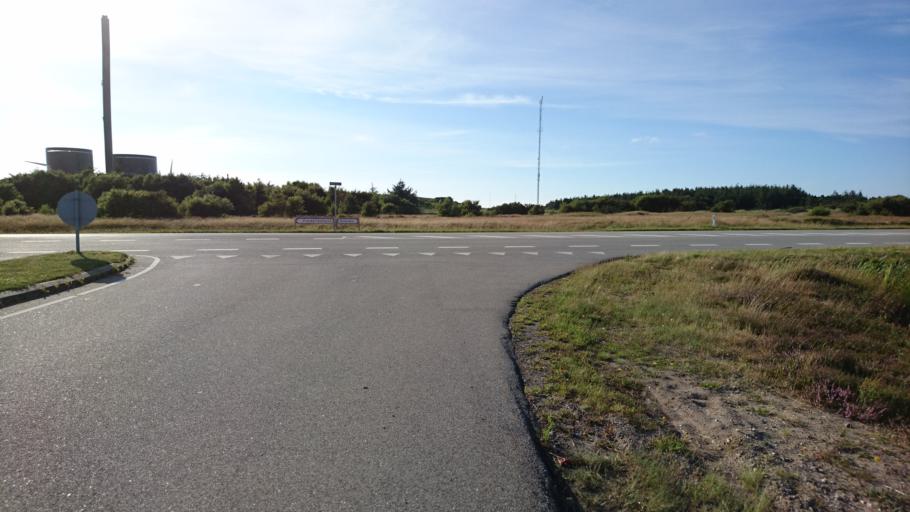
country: DK
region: North Denmark
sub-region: Frederikshavn Kommune
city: Skagen
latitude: 57.7354
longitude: 10.5800
